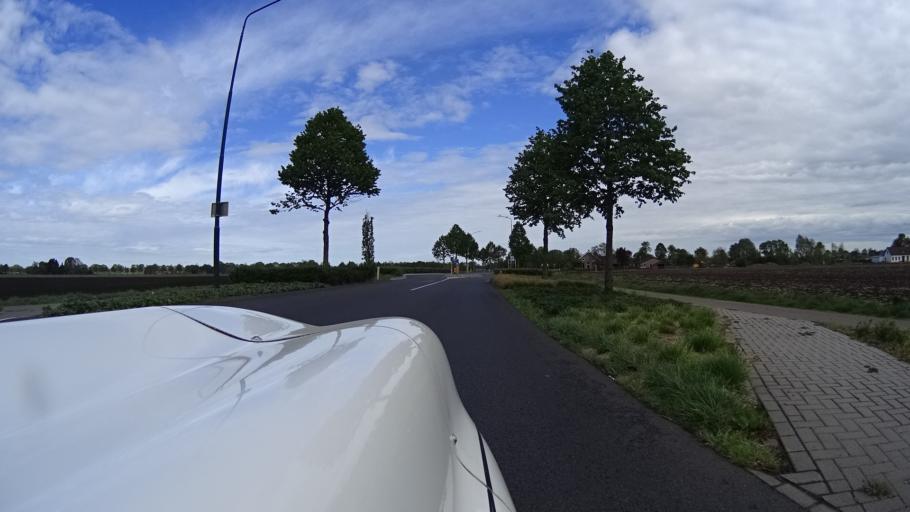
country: NL
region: North Brabant
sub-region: Gemeente Sint Anthonis
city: Sint Anthonis
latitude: 51.6074
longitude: 5.8677
